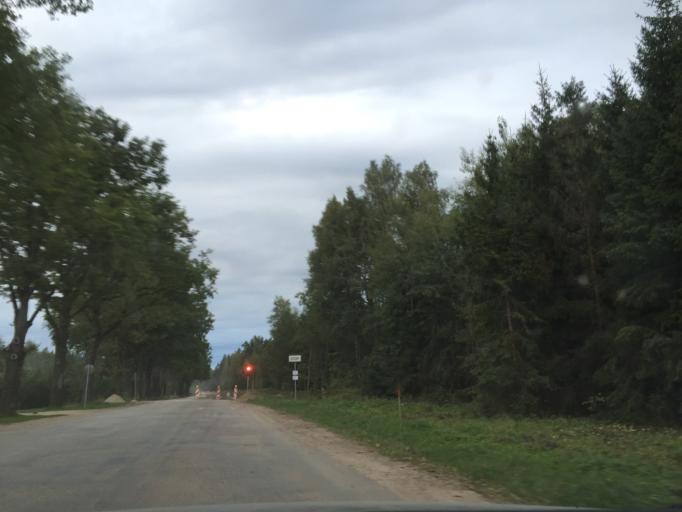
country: LT
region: Panevezys
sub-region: Birzai
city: Birzai
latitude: 56.3904
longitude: 24.6479
